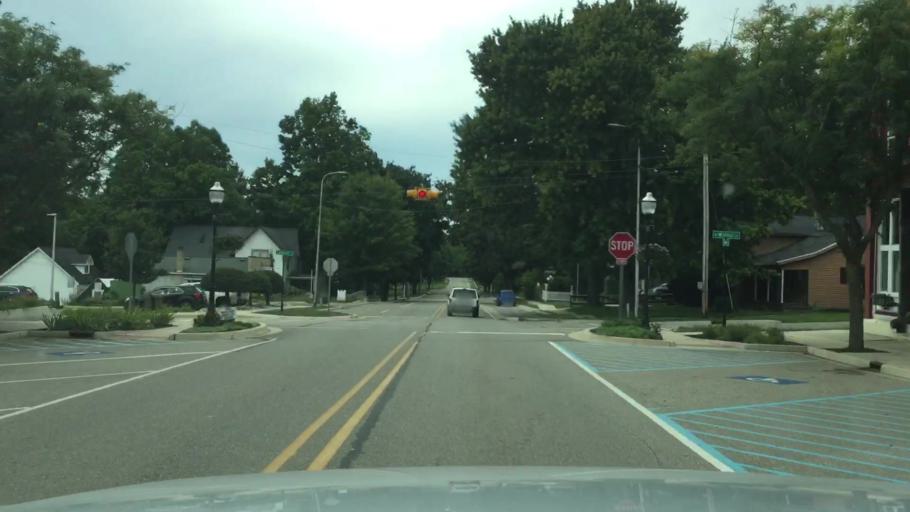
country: US
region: Michigan
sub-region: Shiawassee County
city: Durand
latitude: 42.9392
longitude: -84.0324
